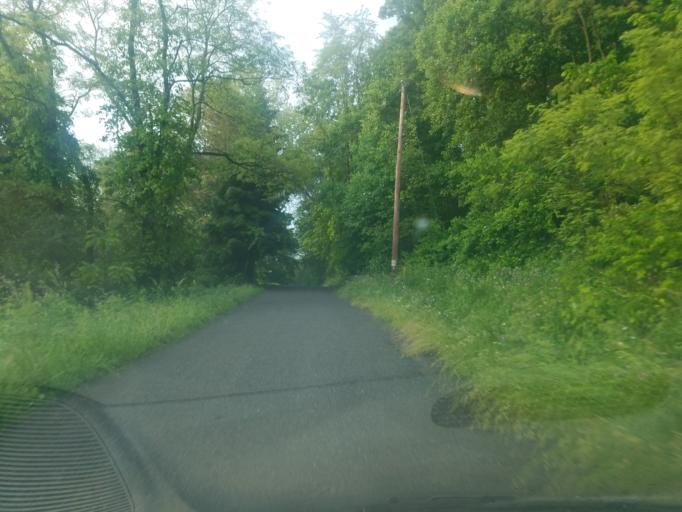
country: US
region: Ohio
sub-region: Stark County
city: Minerva
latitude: 40.7396
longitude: -80.9809
